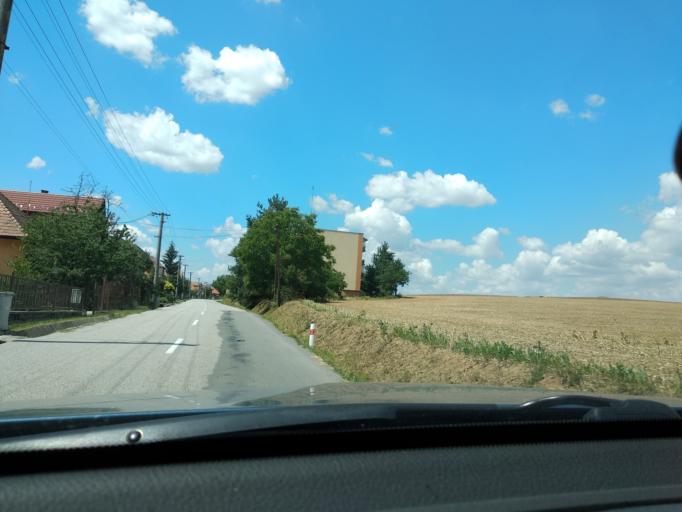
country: SK
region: Nitriansky
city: Banovce nad Bebravou
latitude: 48.6964
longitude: 18.2029
